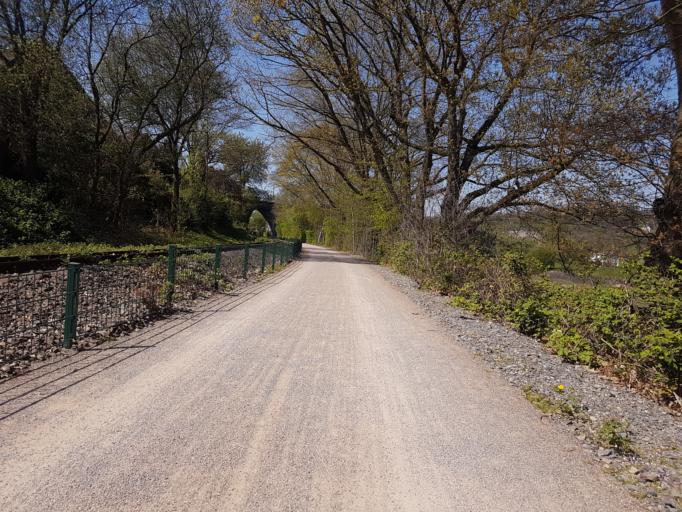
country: DE
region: North Rhine-Westphalia
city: Witten
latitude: 51.4219
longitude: 7.3481
